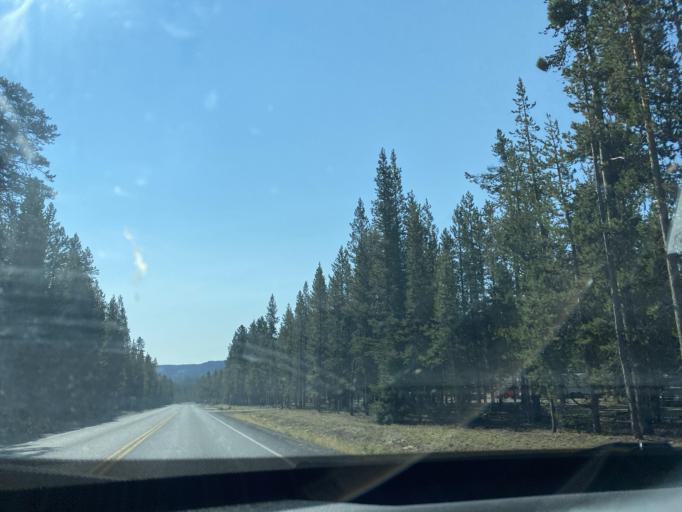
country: US
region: Oregon
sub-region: Deschutes County
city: Three Rivers
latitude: 43.7117
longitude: -121.2765
